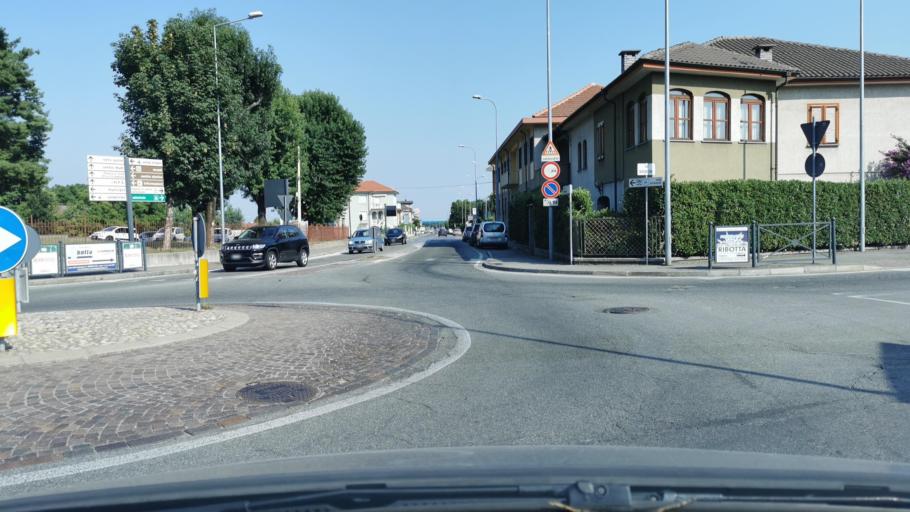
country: IT
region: Piedmont
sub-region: Provincia di Torino
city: Pinerolo
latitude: 44.8849
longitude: 7.3456
